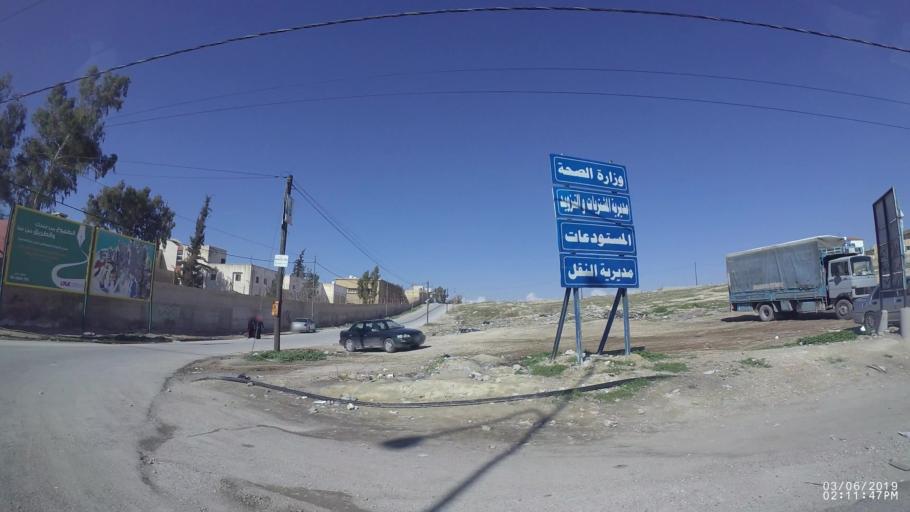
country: JO
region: Zarqa
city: Russeifa
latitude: 32.0301
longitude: 36.0484
